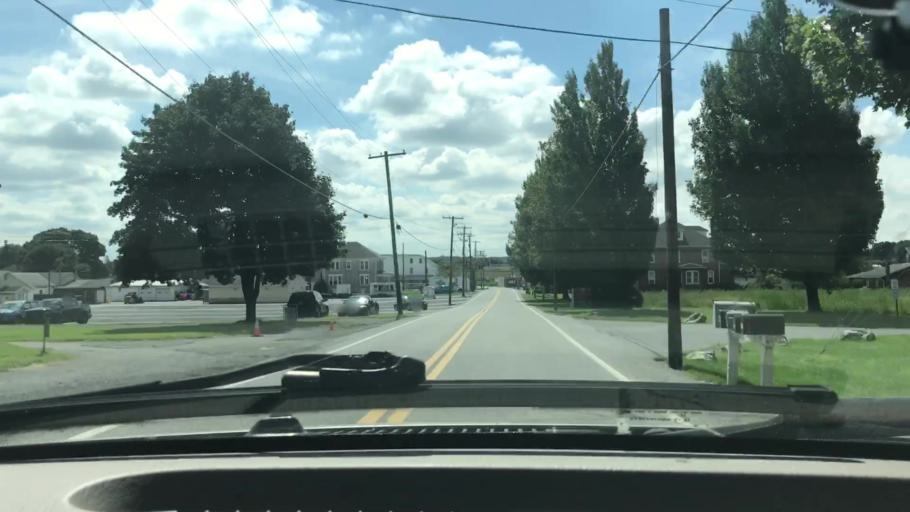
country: US
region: Pennsylvania
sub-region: Lancaster County
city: East Petersburg
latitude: 40.1203
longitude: -76.3793
